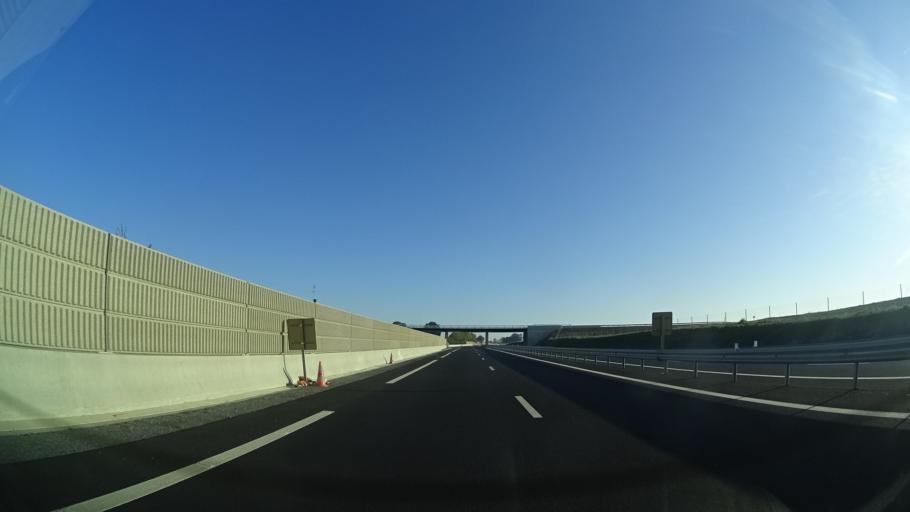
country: FR
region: Brittany
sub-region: Departement d'Ille-et-Vilaine
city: Pipriac
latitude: 47.8017
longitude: -1.9218
